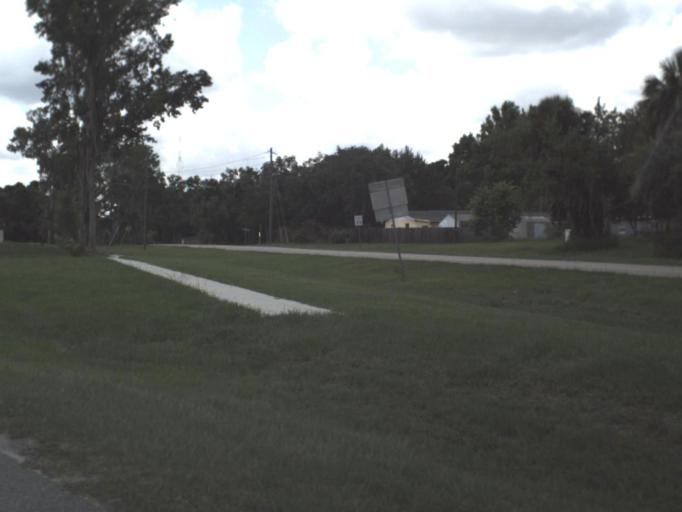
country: US
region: Florida
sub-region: Hernando County
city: Brooksville
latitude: 28.5809
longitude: -82.3757
